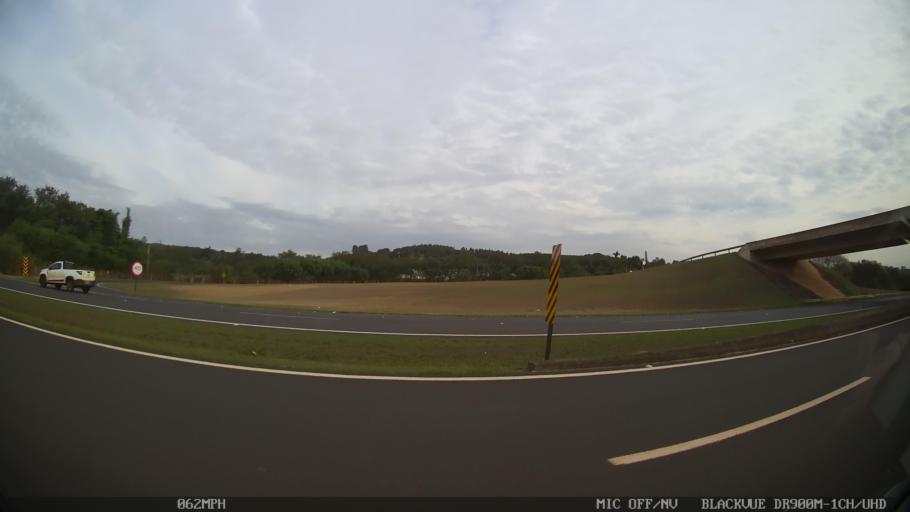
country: BR
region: Sao Paulo
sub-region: Piracicaba
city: Piracicaba
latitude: -22.7002
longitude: -47.6014
